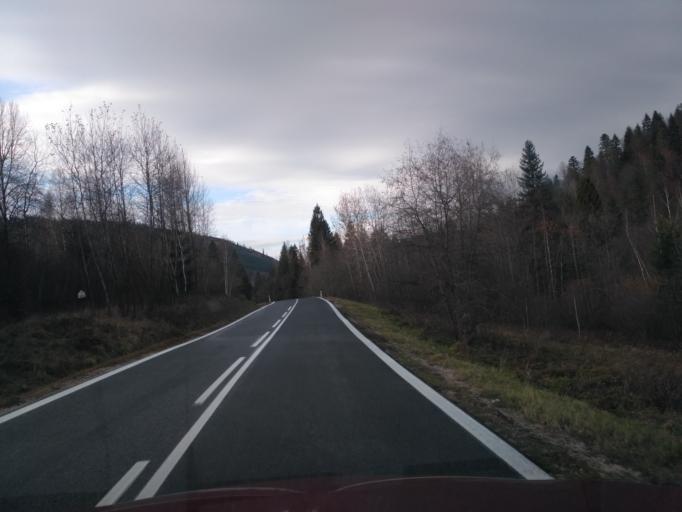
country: SK
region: Kosicky
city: Spisska Nova Ves
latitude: 48.8144
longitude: 20.6685
